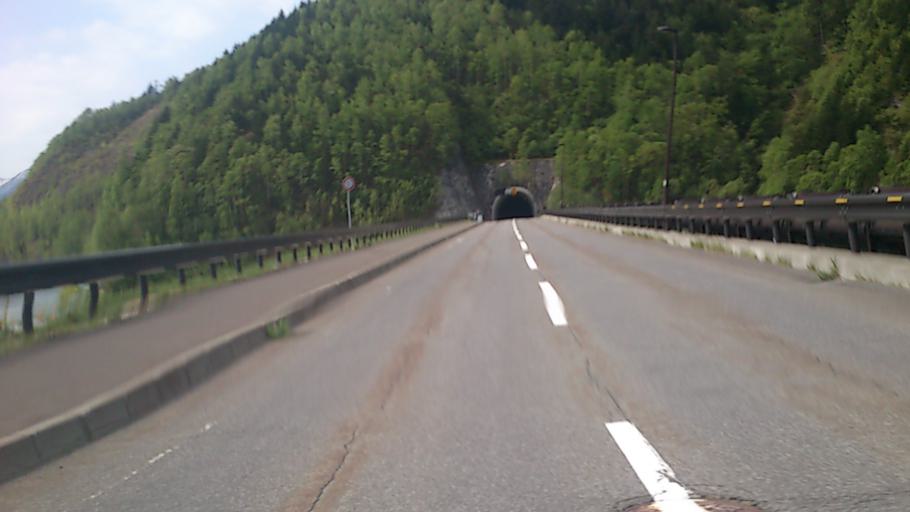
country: JP
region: Hokkaido
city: Kamikawa
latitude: 43.6766
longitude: 143.0366
